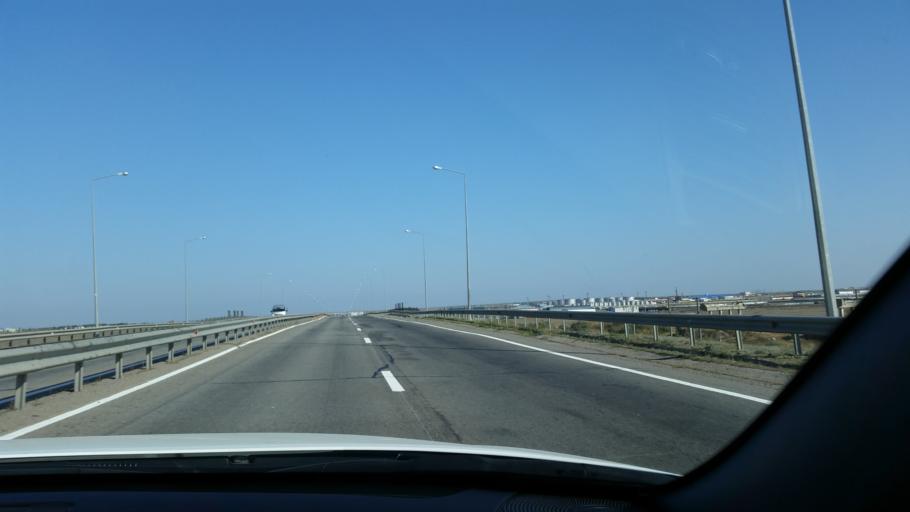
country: KZ
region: Astana Qalasy
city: Astana
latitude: 51.2514
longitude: 71.3480
